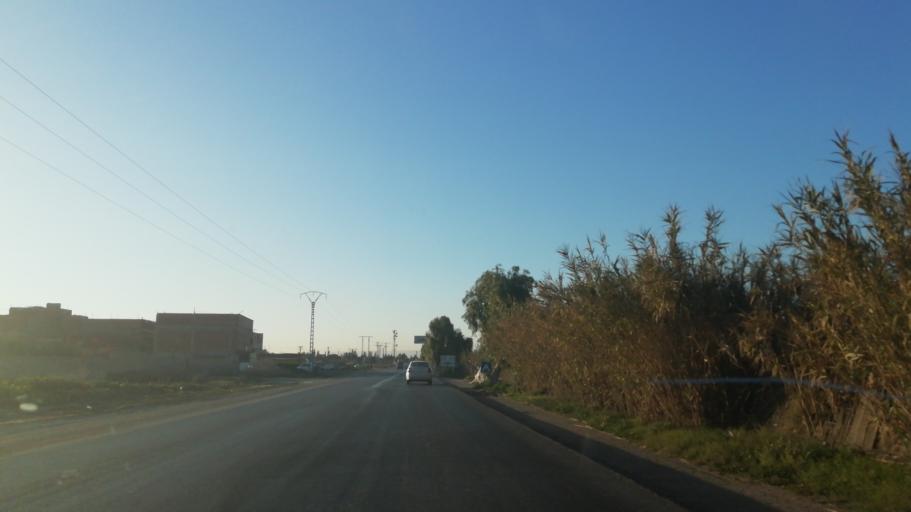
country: DZ
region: Relizane
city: Relizane
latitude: 35.7648
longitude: 0.6418
